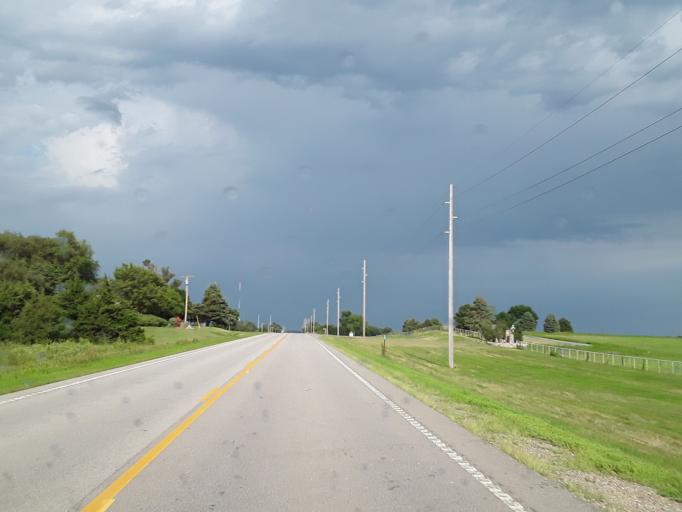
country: US
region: Nebraska
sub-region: Saunders County
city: Ashland
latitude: 41.0887
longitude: -96.4019
